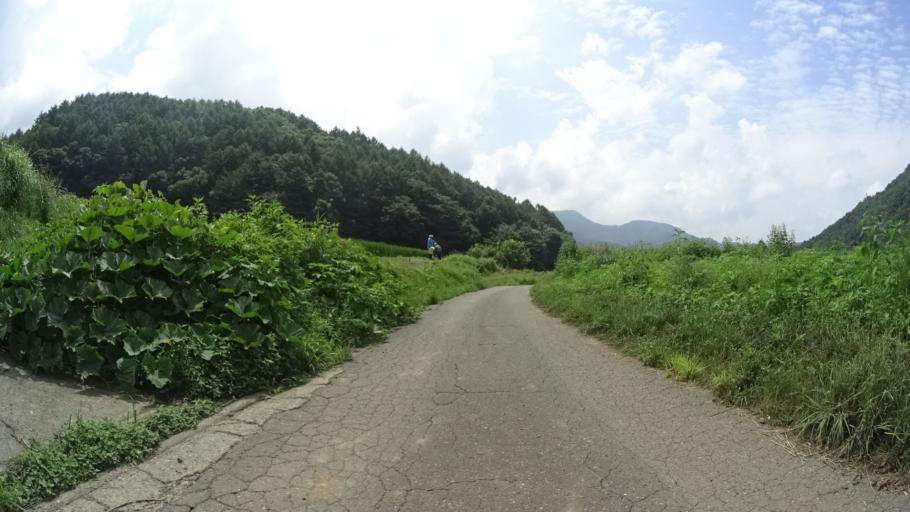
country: JP
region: Yamanashi
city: Nirasaki
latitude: 35.9011
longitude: 138.4709
